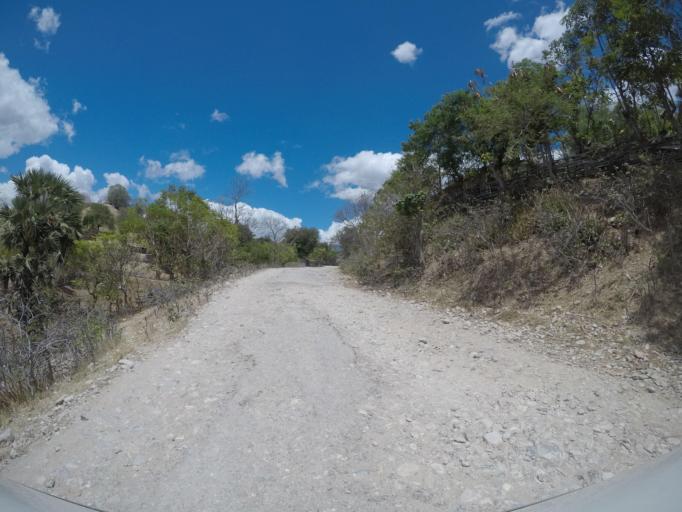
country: TL
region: Baucau
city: Baucau
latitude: -8.4756
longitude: 126.6009
